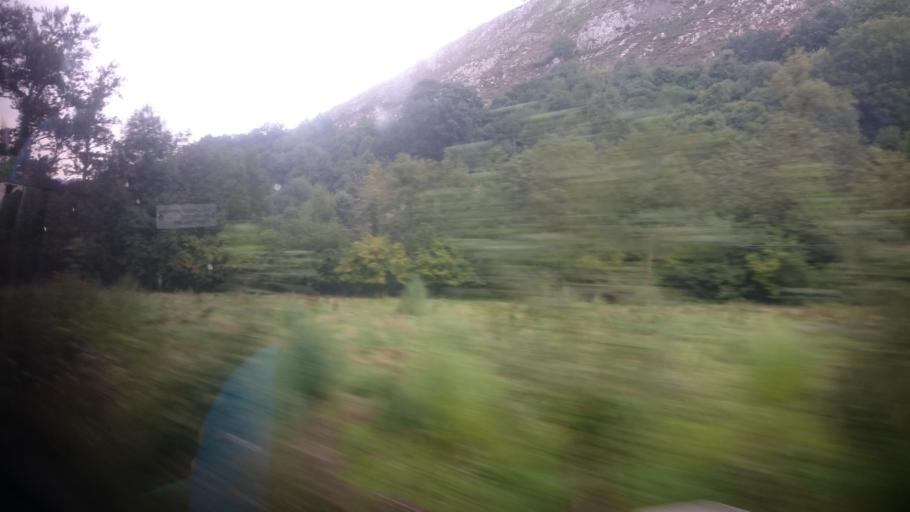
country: ES
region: Asturias
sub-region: Province of Asturias
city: Cangas de Onis
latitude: 43.3211
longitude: -5.0756
